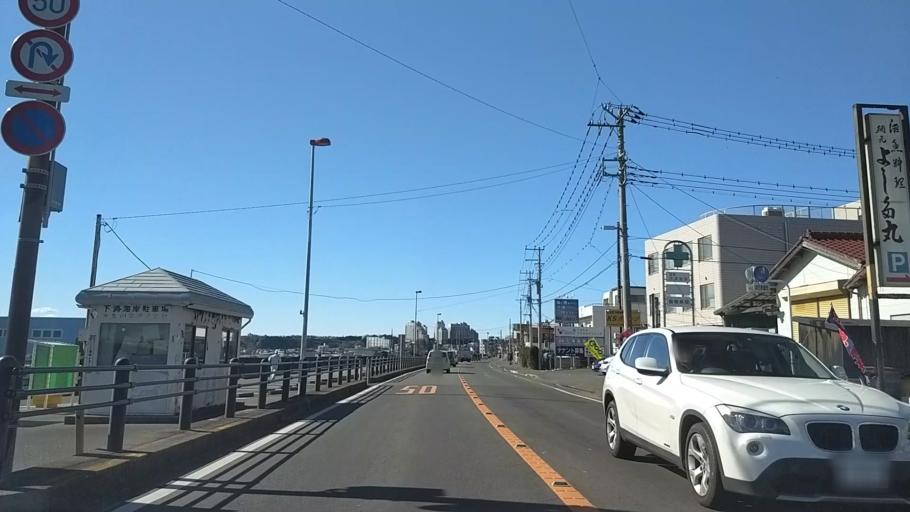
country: JP
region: Kanagawa
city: Miura
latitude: 35.1919
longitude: 139.6626
